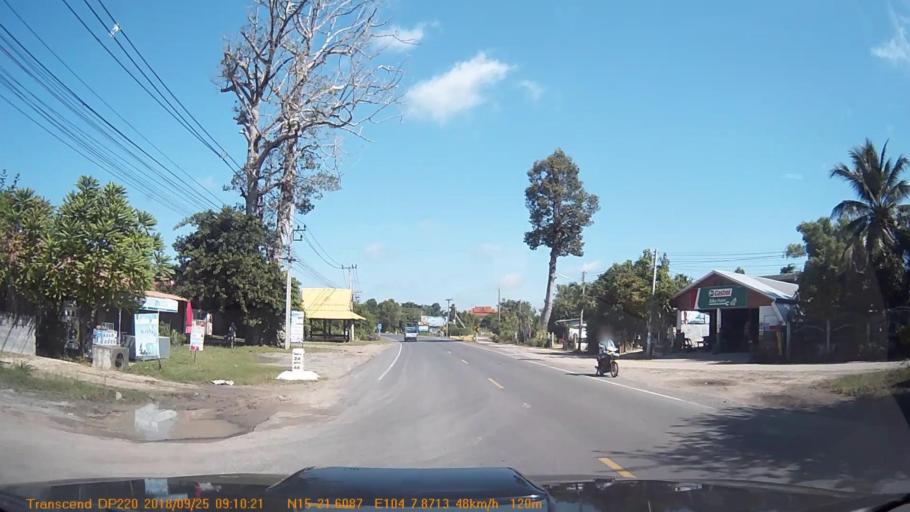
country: TH
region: Sisaket
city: Rasi Salai
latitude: 15.3600
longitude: 104.1313
